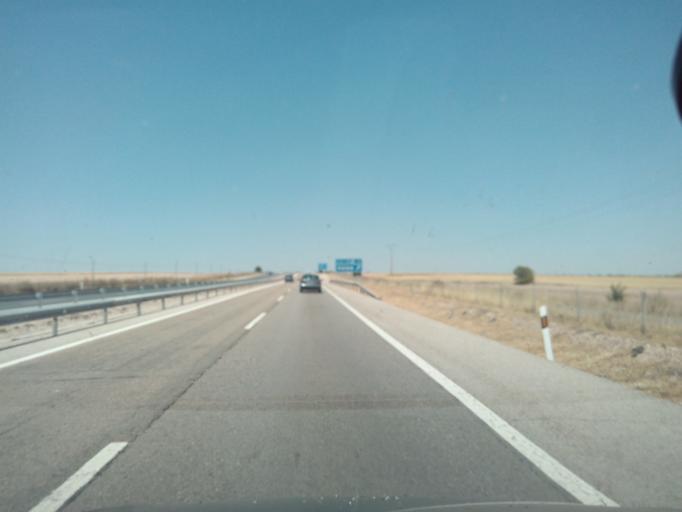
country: ES
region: Castille-La Mancha
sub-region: Province of Toledo
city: Tembleque
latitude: 39.7509
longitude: -3.4848
